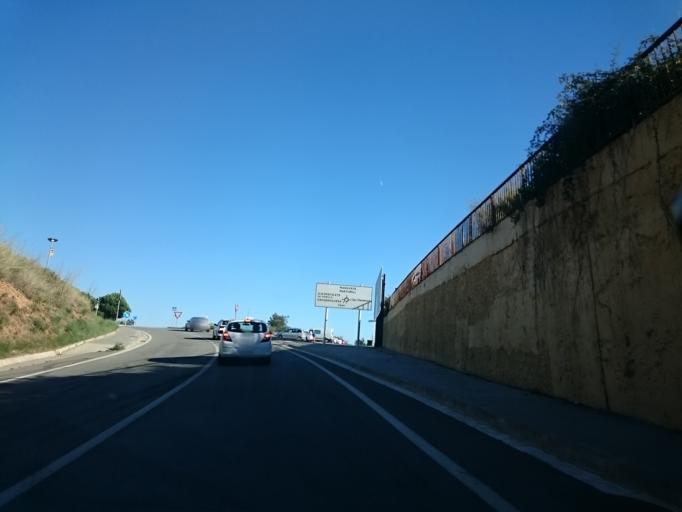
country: ES
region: Catalonia
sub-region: Provincia de Barcelona
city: Piera
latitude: 41.5198
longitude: 1.7589
